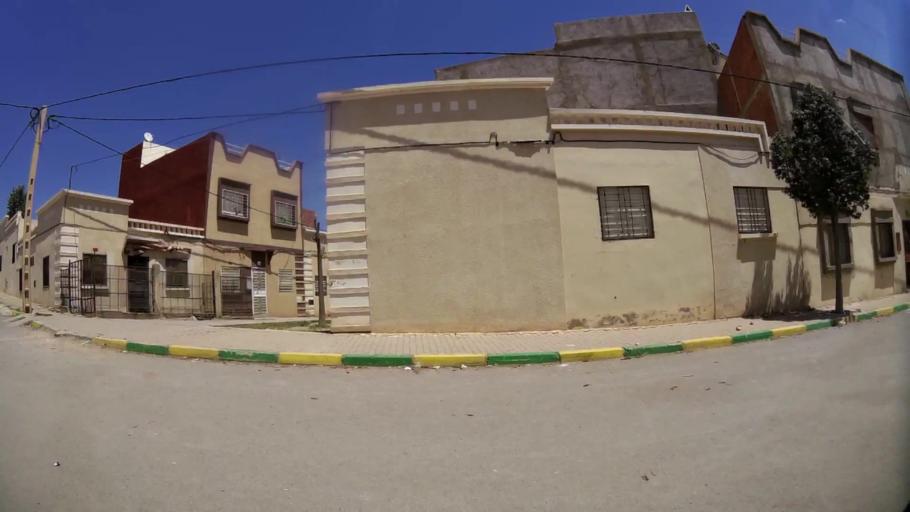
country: MA
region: Oriental
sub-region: Oujda-Angad
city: Oujda
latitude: 34.6883
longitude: -1.9506
